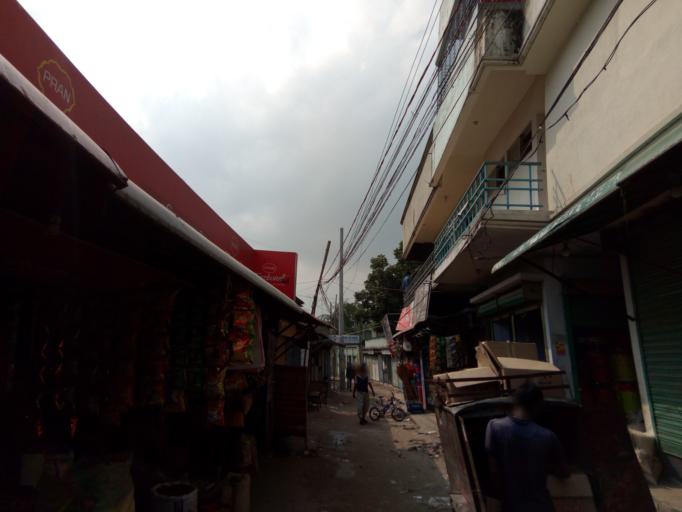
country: BD
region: Dhaka
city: Paltan
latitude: 23.7594
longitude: 90.4617
